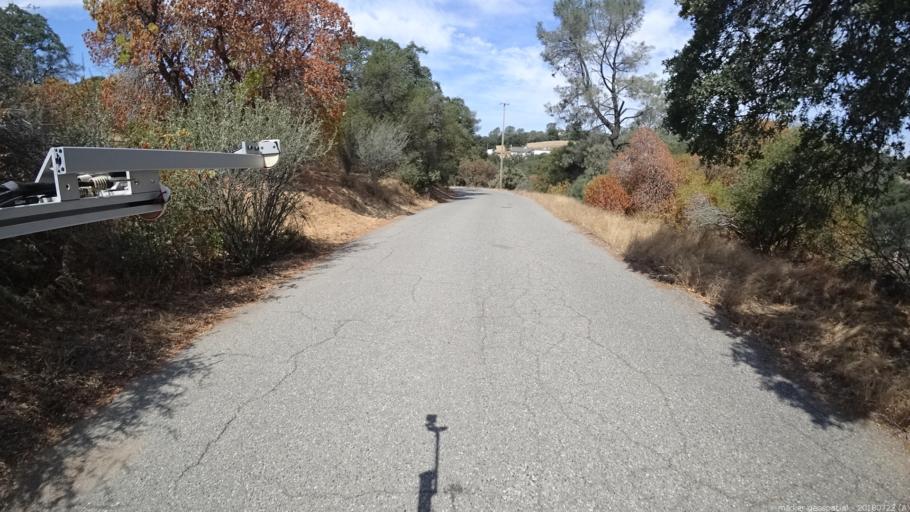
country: US
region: California
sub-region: Madera County
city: Coarsegold
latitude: 37.2581
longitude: -119.7146
